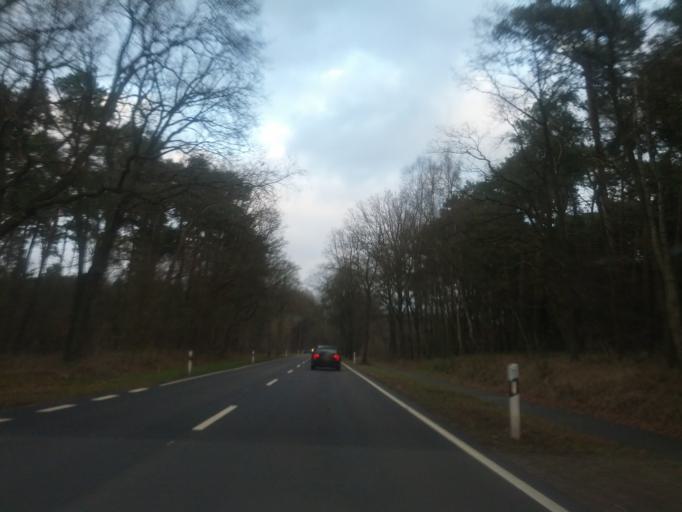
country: DE
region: Lower Saxony
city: Hemsbunde
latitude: 53.1384
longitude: 9.4522
